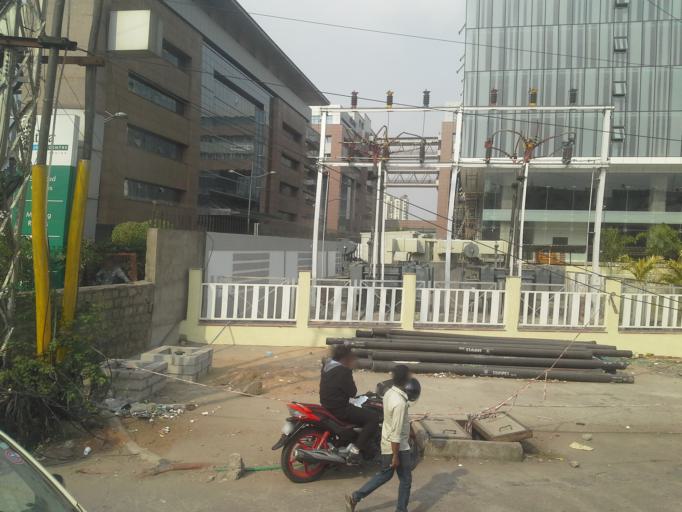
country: IN
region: Telangana
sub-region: Rangareddi
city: Kukatpalli
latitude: 17.4578
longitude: 78.3727
